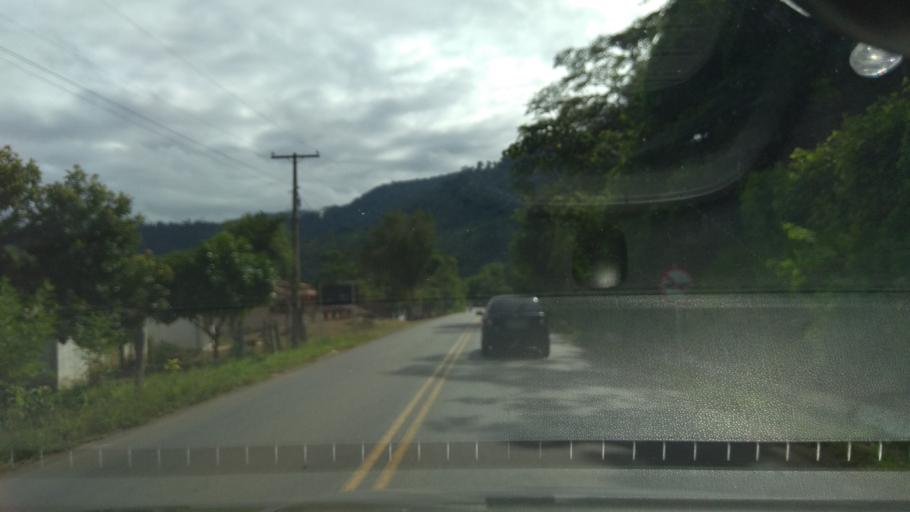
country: BR
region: Bahia
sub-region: Ubaira
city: Ubaira
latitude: -13.2613
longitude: -39.6181
